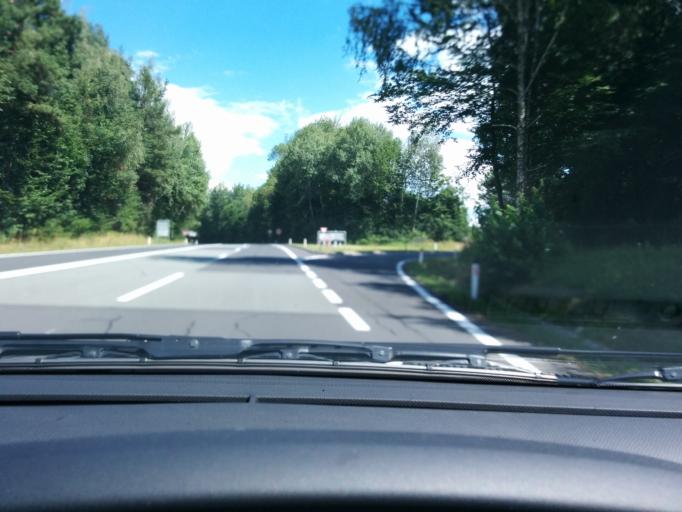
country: AT
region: Styria
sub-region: Politischer Bezirk Hartberg-Fuerstenfeld
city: Grafendorf bei Hartberg
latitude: 47.3412
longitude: 16.0022
